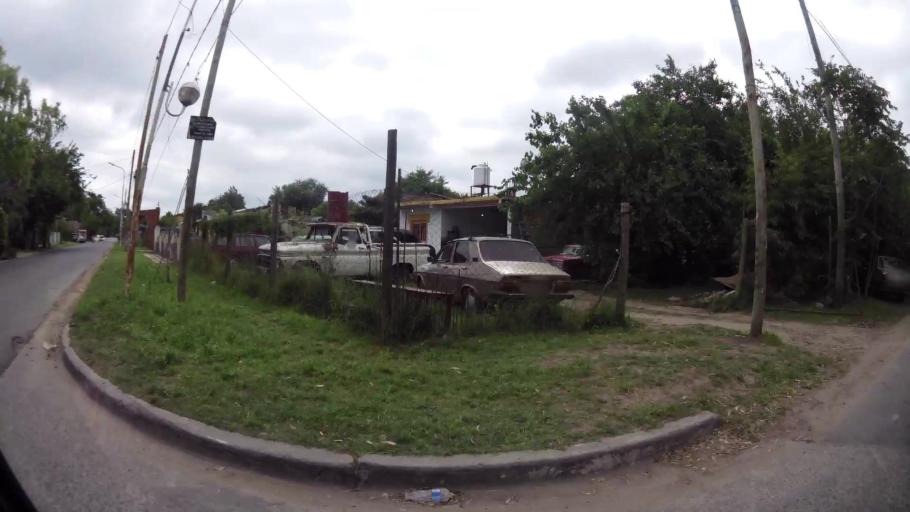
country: AR
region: Buenos Aires
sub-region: Partido de Ezeiza
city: Ezeiza
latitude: -34.8431
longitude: -58.5105
